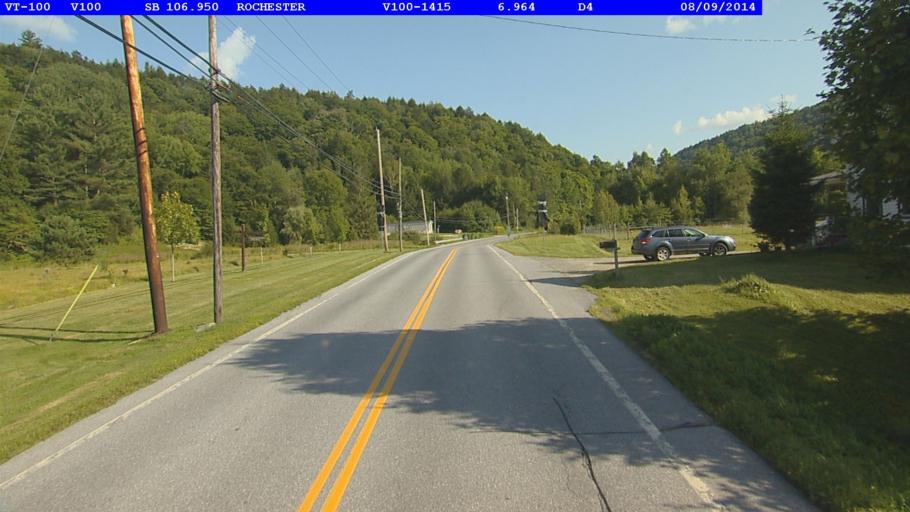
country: US
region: Vermont
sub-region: Orange County
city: Randolph
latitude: 43.8953
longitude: -72.8192
